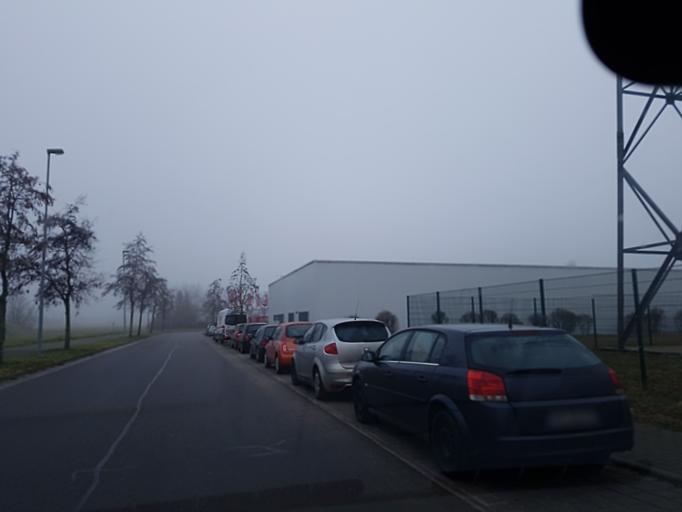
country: DE
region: Brandenburg
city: Finsterwalde
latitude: 51.6335
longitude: 13.7355
